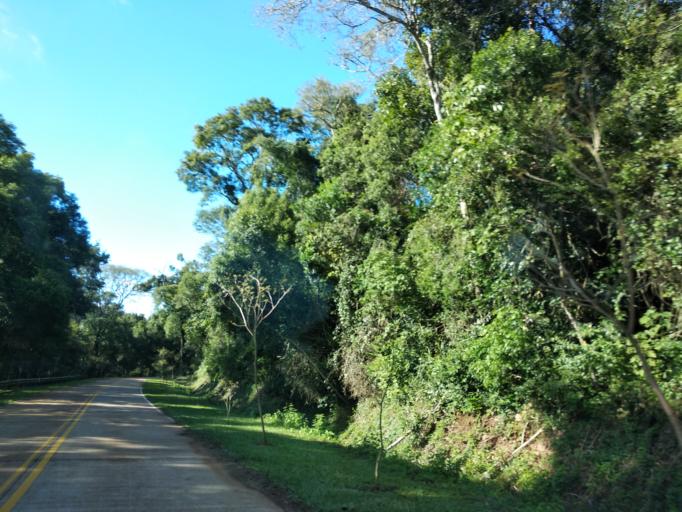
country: AR
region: Misiones
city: Cerro Cora
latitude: -27.4539
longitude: -55.5659
